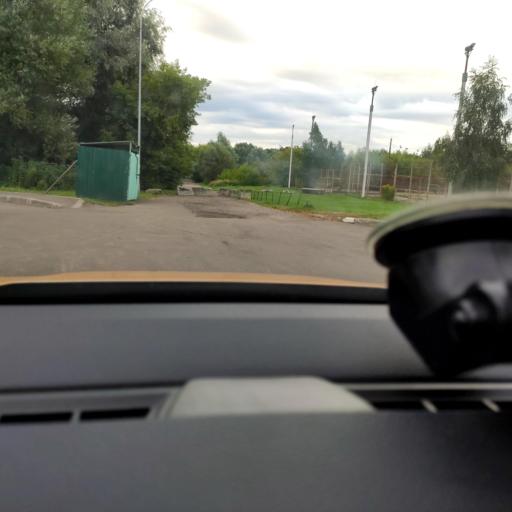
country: RU
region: Moscow
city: Vatutino
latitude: 55.8538
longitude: 37.6961
